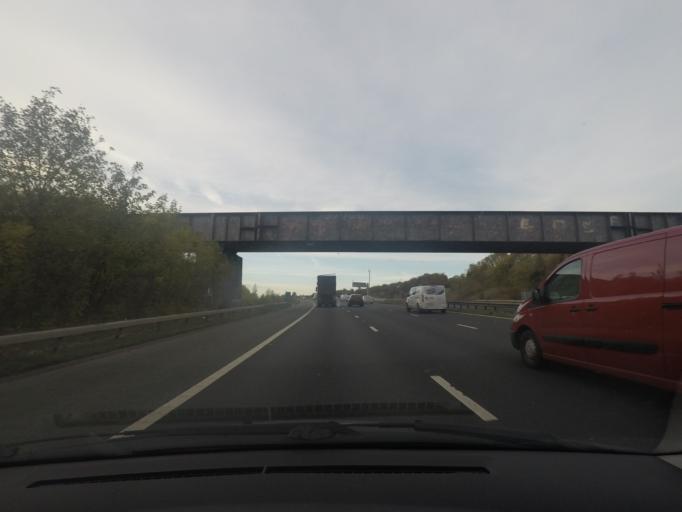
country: GB
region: England
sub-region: Barnsley
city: Dodworth
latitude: 53.5495
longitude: -1.5167
